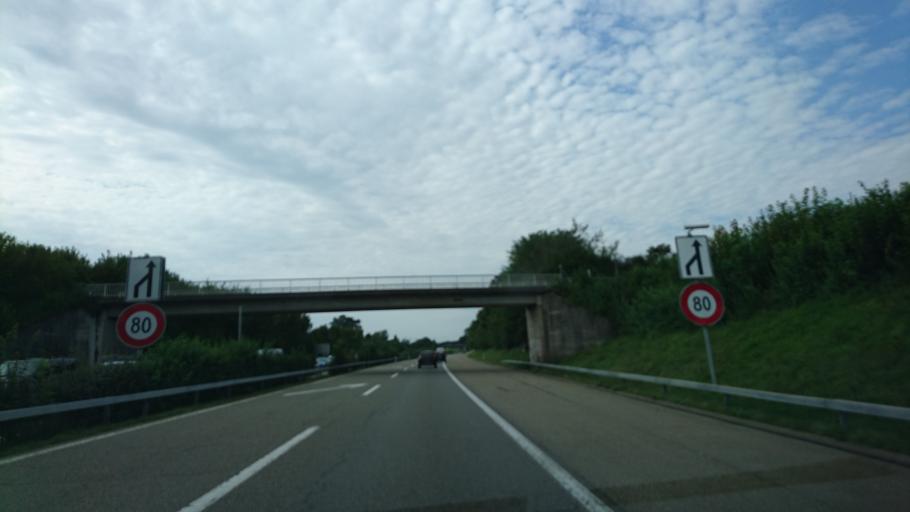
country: CH
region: Zurich
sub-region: Bezirk Hinwil
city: Bubikon
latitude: 47.2819
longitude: 8.8235
